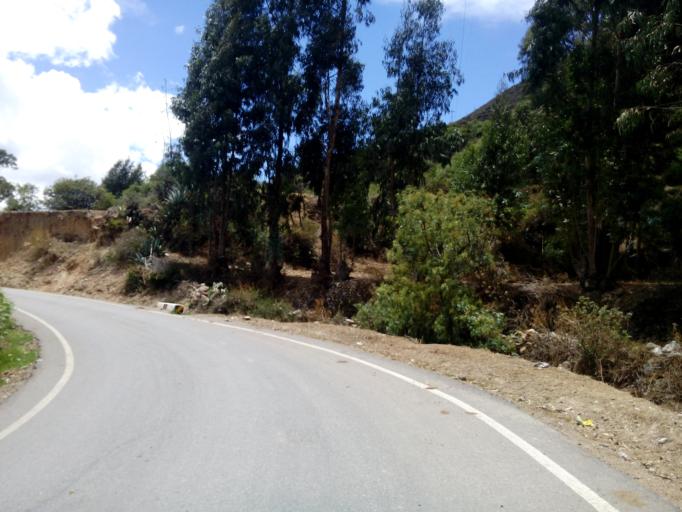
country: PE
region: Ayacucho
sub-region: Provincia de Victor Fajardo
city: Canaria
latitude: -13.8775
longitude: -73.9388
